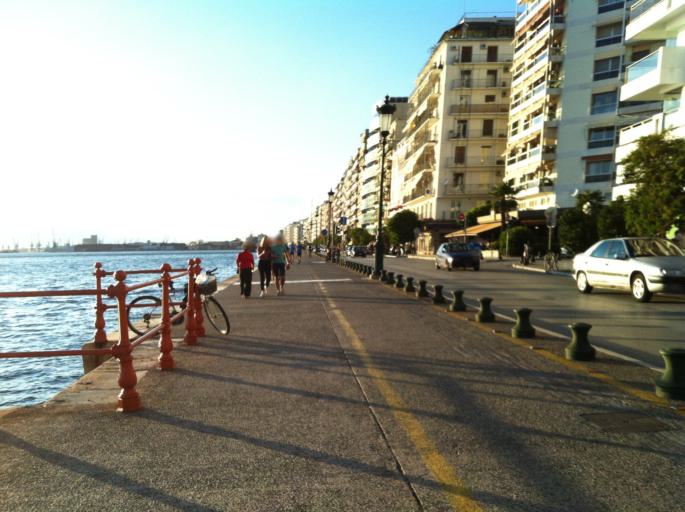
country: GR
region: Central Macedonia
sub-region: Nomos Thessalonikis
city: Agios Pavlos
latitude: 40.6278
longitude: 22.9467
